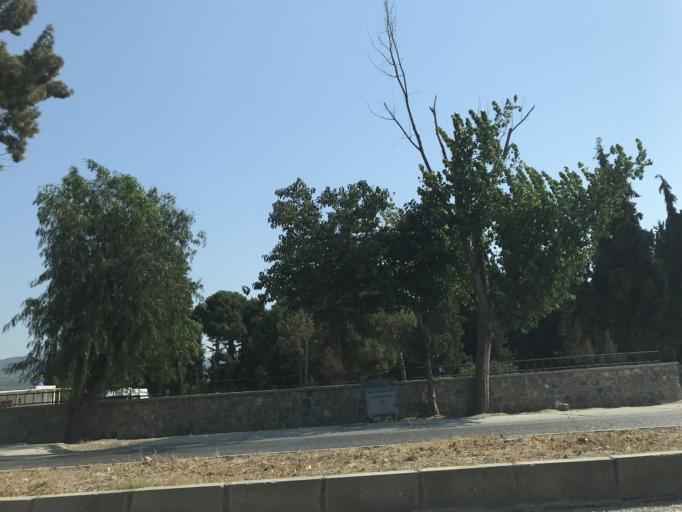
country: TR
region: Izmir
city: Selcuk
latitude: 37.9487
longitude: 27.3607
